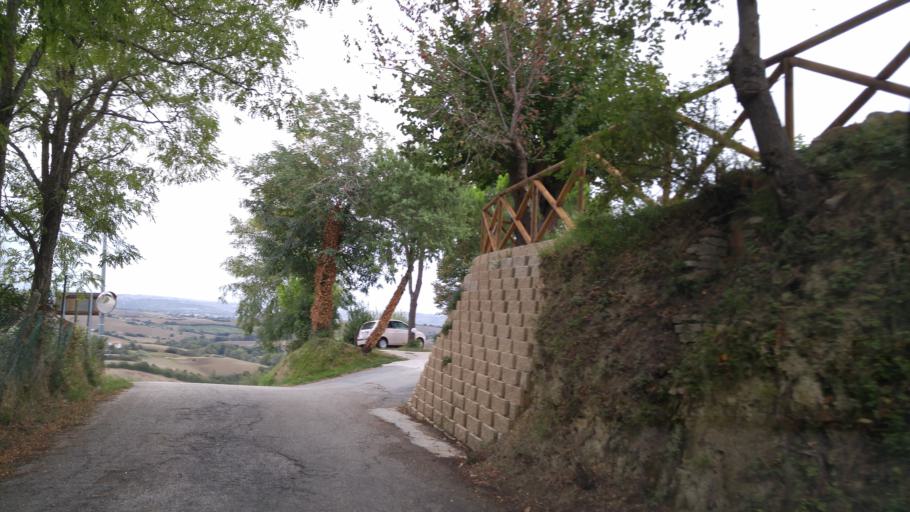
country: IT
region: The Marches
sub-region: Provincia di Pesaro e Urbino
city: Mombaroccio
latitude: 43.7923
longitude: 12.8746
